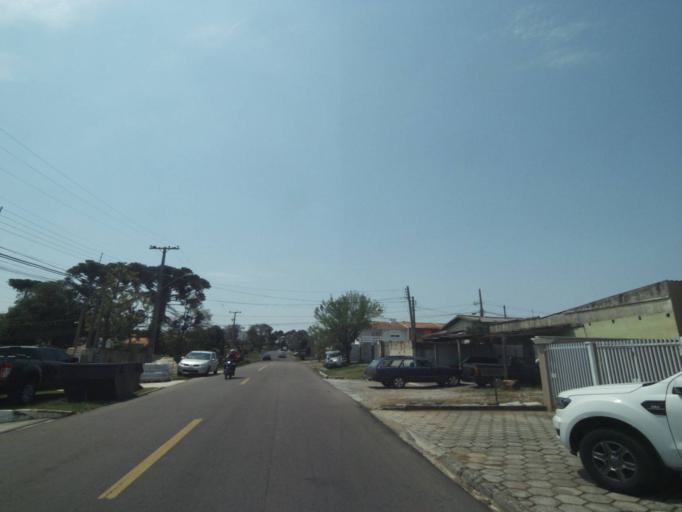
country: BR
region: Parana
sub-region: Sao Jose Dos Pinhais
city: Sao Jose dos Pinhais
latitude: -25.5179
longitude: -49.2642
